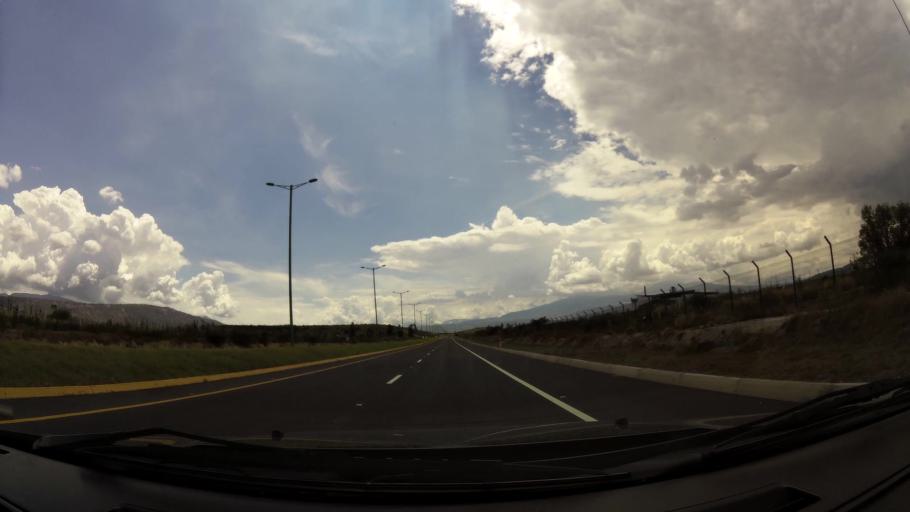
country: EC
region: Pichincha
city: Quito
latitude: -0.1164
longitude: -78.3654
